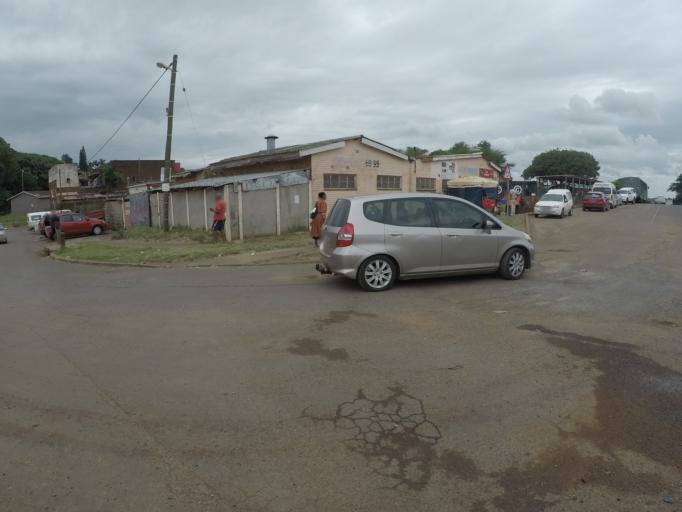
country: ZA
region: KwaZulu-Natal
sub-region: uThungulu District Municipality
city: Empangeni
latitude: -28.7740
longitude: 31.8621
